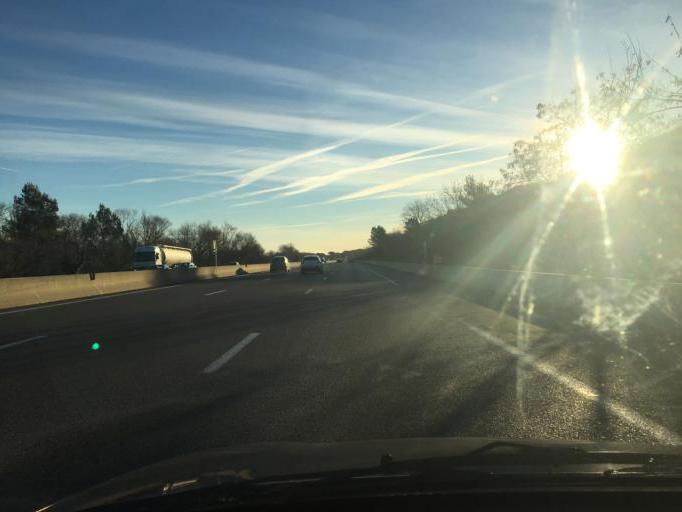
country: FR
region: Provence-Alpes-Cote d'Azur
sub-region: Departement du Var
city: Le Muy
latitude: 43.4610
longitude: 6.5919
